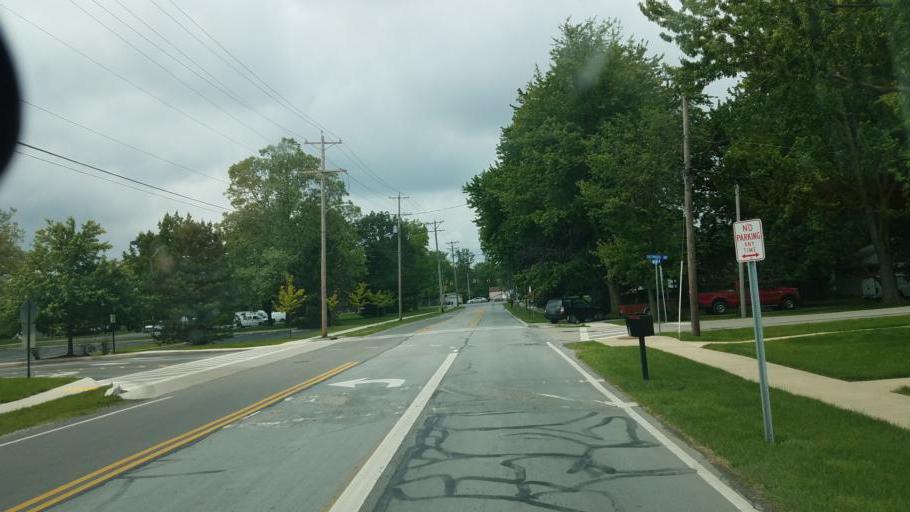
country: US
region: Ohio
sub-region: Delaware County
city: Delaware
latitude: 40.3138
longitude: -83.0879
